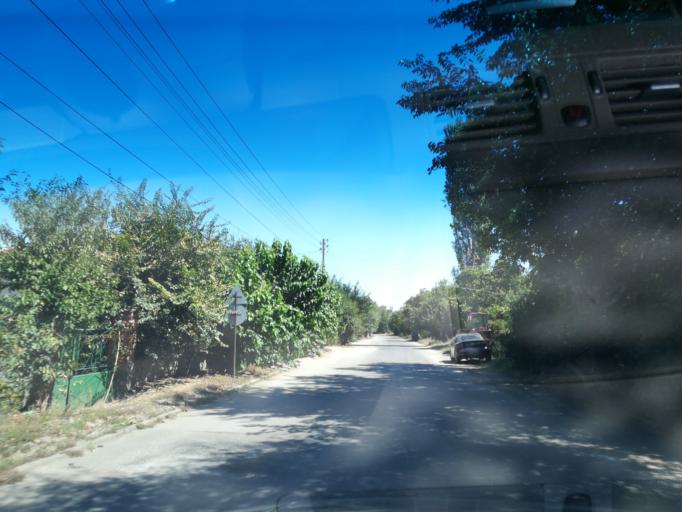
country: BG
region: Pazardzhik
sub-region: Obshtina Pazardzhik
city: Pazardzhik
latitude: 42.2516
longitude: 24.4311
